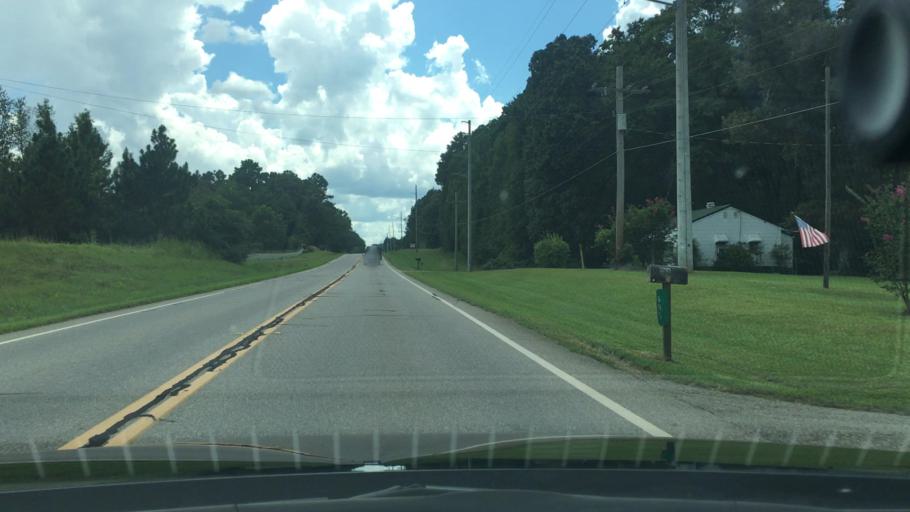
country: US
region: Georgia
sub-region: Putnam County
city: Eatonton
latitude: 33.3699
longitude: -83.3304
